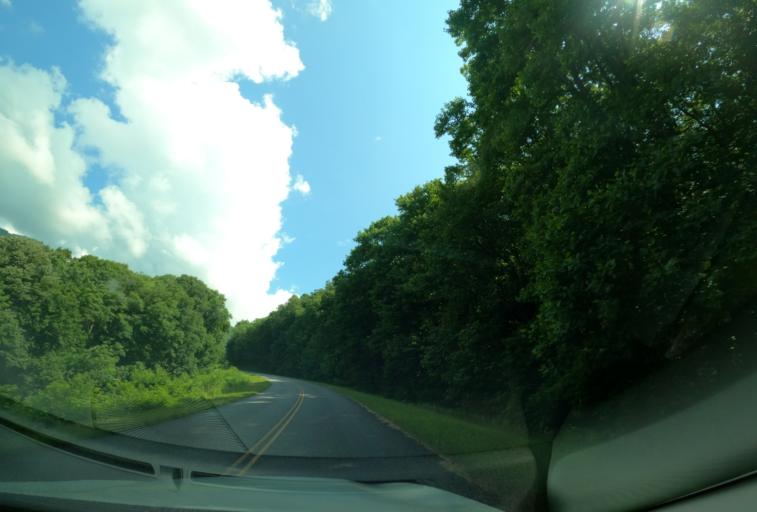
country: US
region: North Carolina
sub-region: Haywood County
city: Maggie Valley
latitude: 35.4444
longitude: -83.0941
